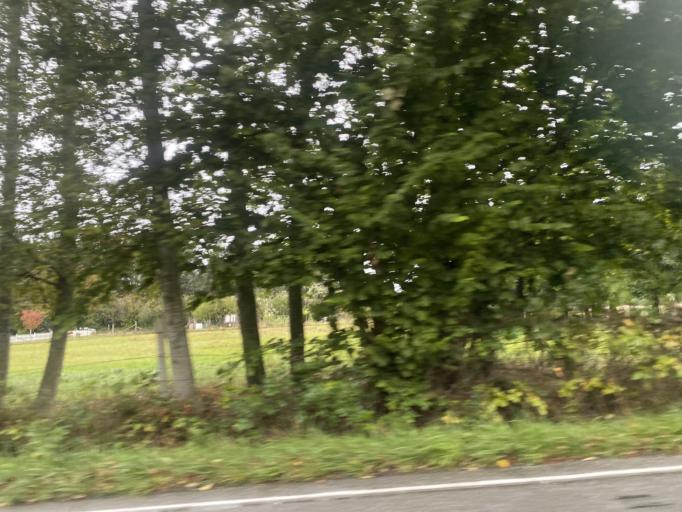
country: US
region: Washington
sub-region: Island County
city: Freeland
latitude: 48.0803
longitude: -122.4854
